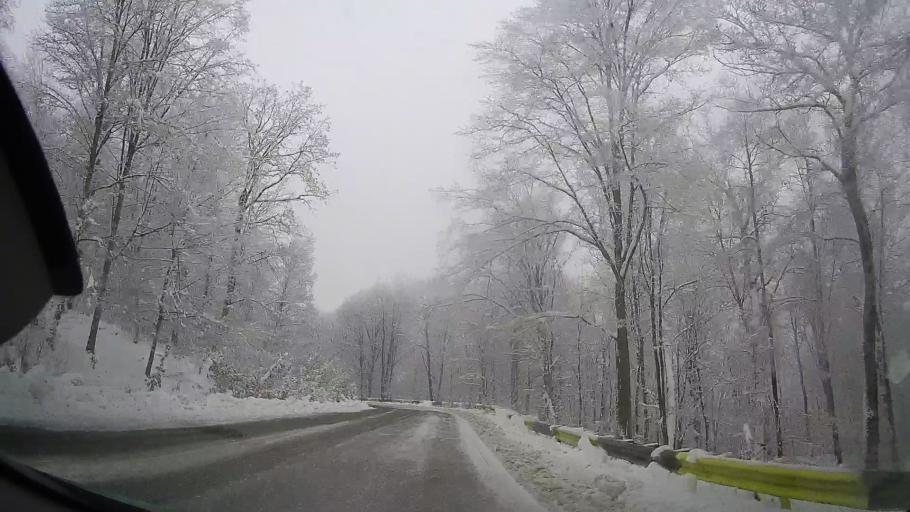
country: RO
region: Neamt
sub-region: Comuna Valea Ursului
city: Valea Ursului
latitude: 46.8397
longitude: 27.0691
